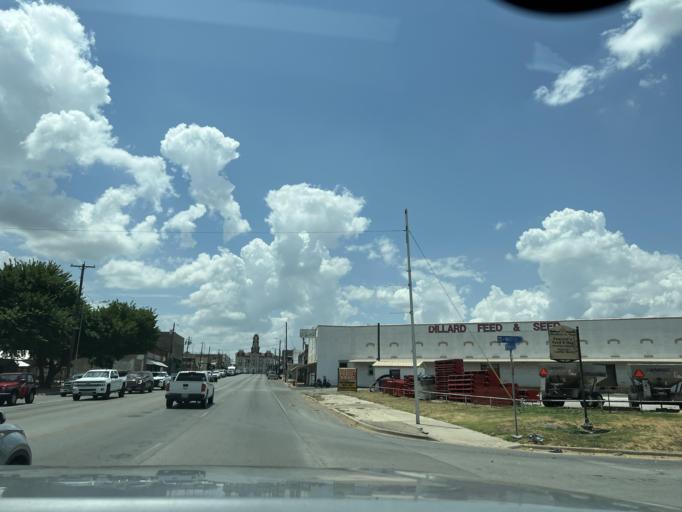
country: US
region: Texas
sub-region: Parker County
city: Weatherford
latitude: 32.7631
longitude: -97.7974
